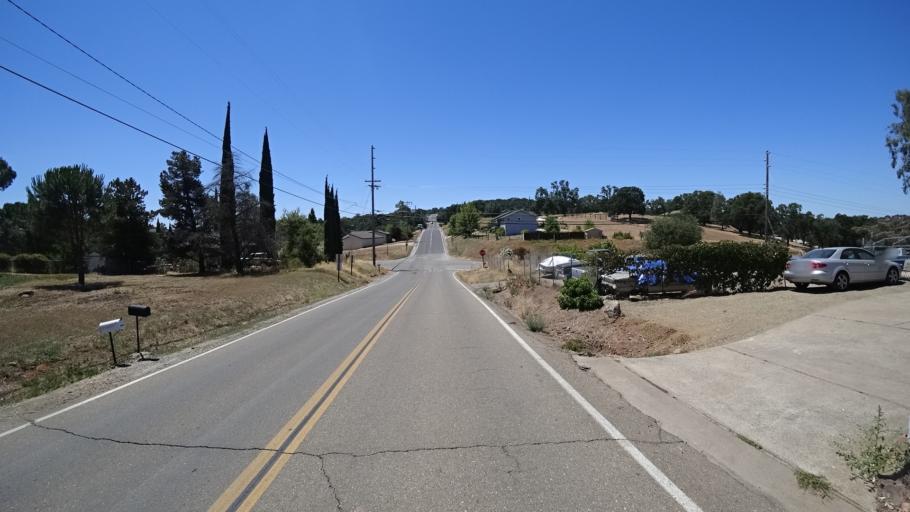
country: US
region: California
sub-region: Calaveras County
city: Valley Springs
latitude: 38.1582
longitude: -120.8395
